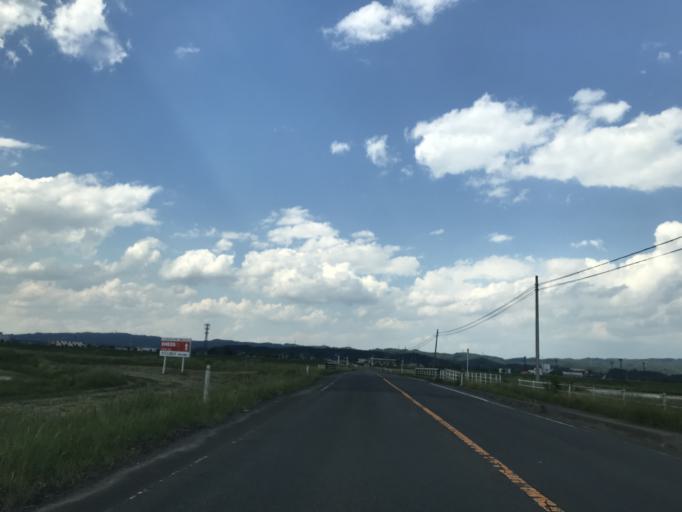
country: JP
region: Miyagi
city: Wakuya
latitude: 38.5246
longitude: 141.1306
